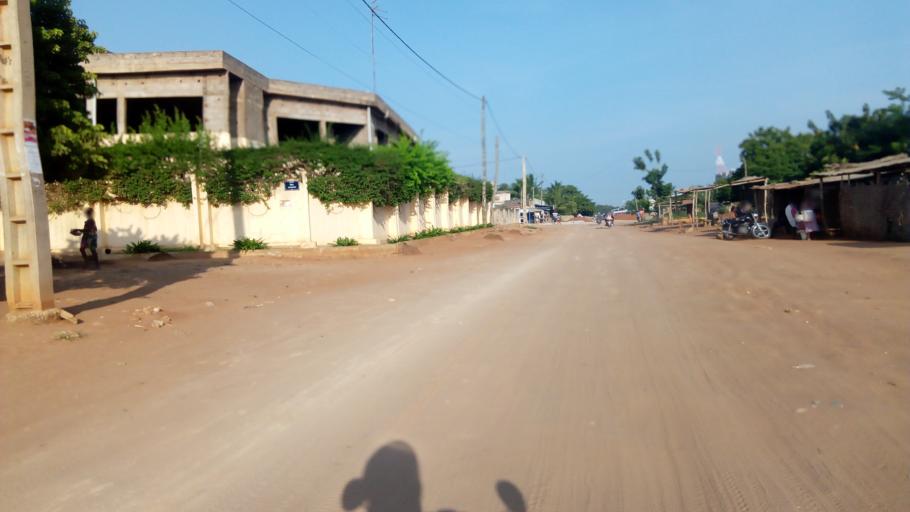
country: TG
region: Maritime
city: Lome
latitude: 6.1839
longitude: 1.1811
